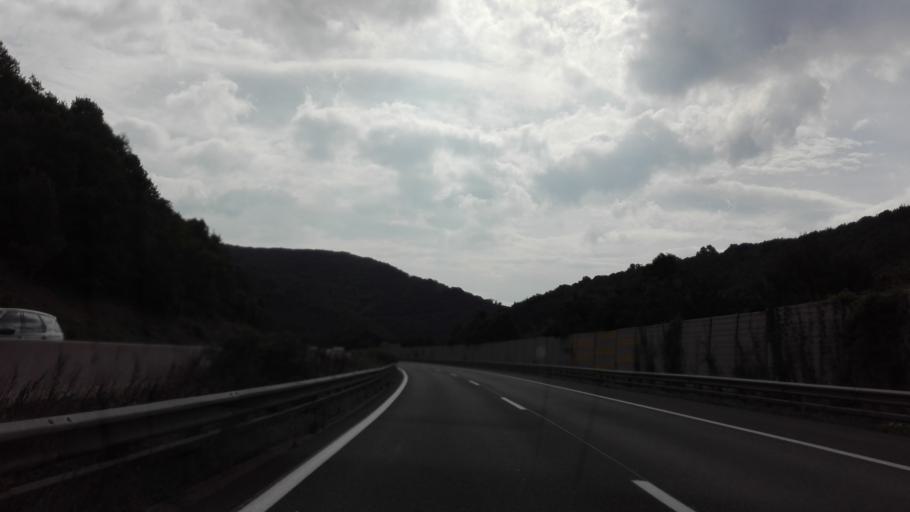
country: AT
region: Lower Austria
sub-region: Politischer Bezirk Baden
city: Klausen-Leopoldsdorf
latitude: 48.0819
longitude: 16.0401
